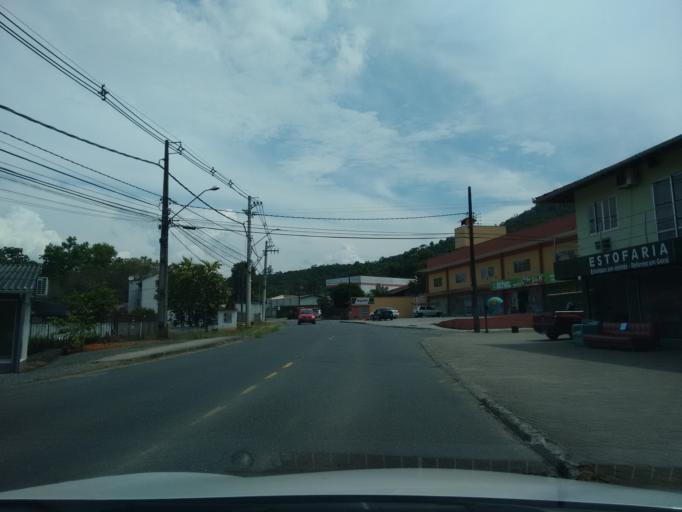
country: BR
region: Santa Catarina
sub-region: Blumenau
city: Blumenau
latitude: -26.9144
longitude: -49.1344
